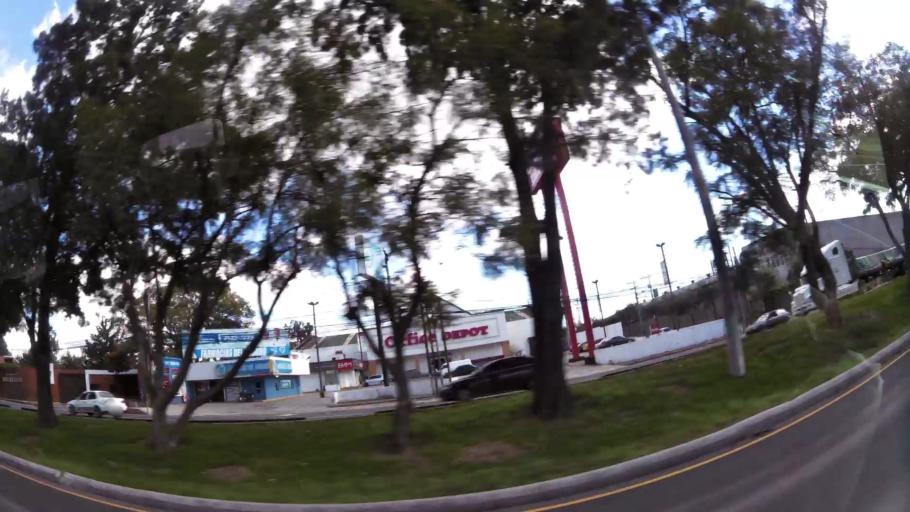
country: GT
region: Guatemala
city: Villa Nueva
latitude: 14.5836
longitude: -90.5659
